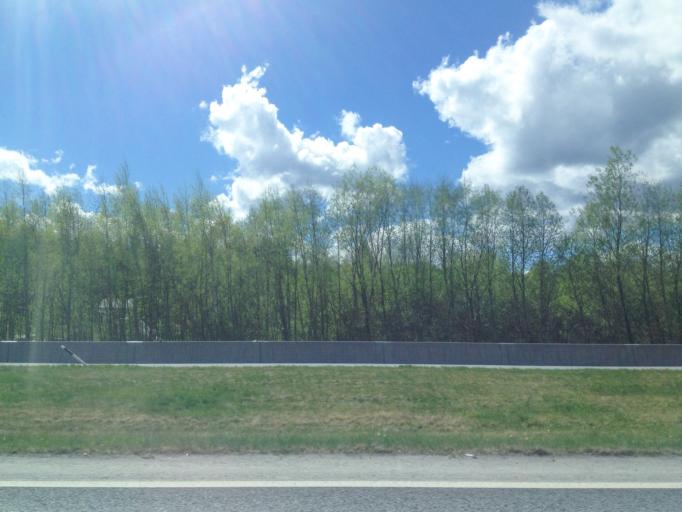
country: FI
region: Haeme
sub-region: Haemeenlinna
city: Parola
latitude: 61.0317
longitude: 24.3919
